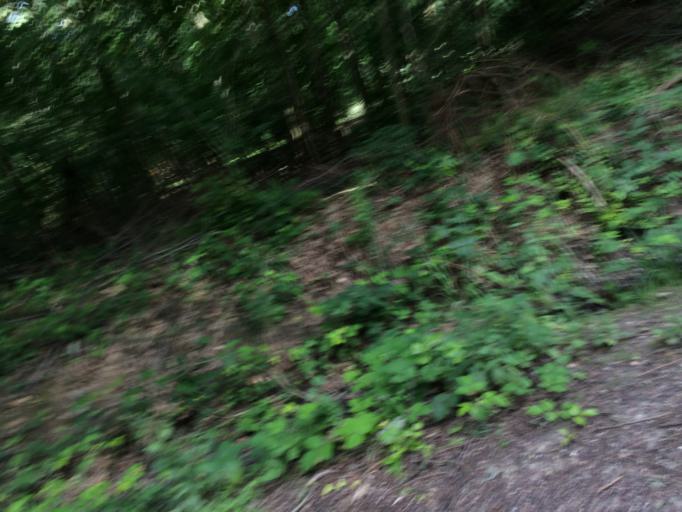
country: FR
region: Ile-de-France
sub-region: Departement de l'Essonne
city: Etiolles
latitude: 48.6563
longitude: 2.4790
